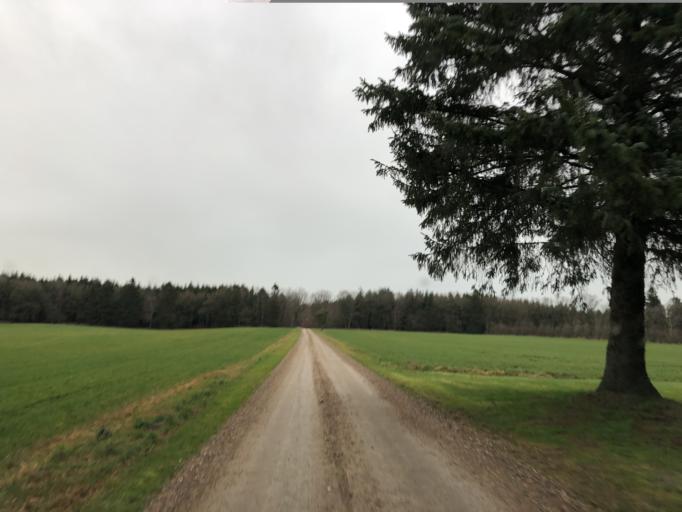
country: DK
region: Central Jutland
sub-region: Holstebro Kommune
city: Vinderup
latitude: 56.3779
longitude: 8.8645
